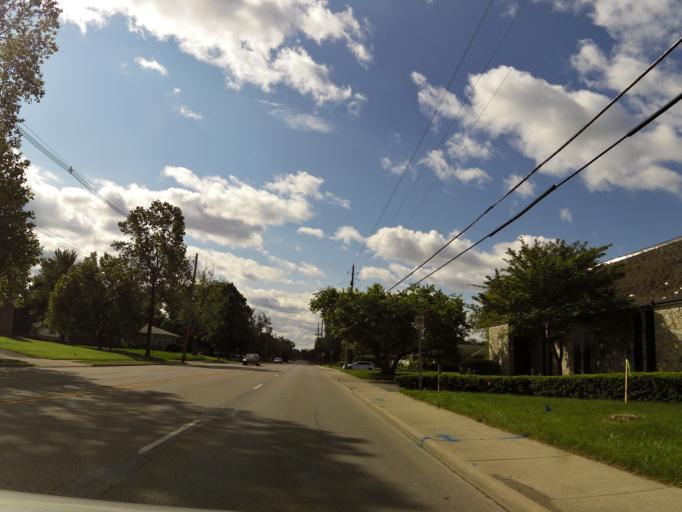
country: US
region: Ohio
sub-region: Franklin County
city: Bexley
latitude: 39.9442
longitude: -82.9346
